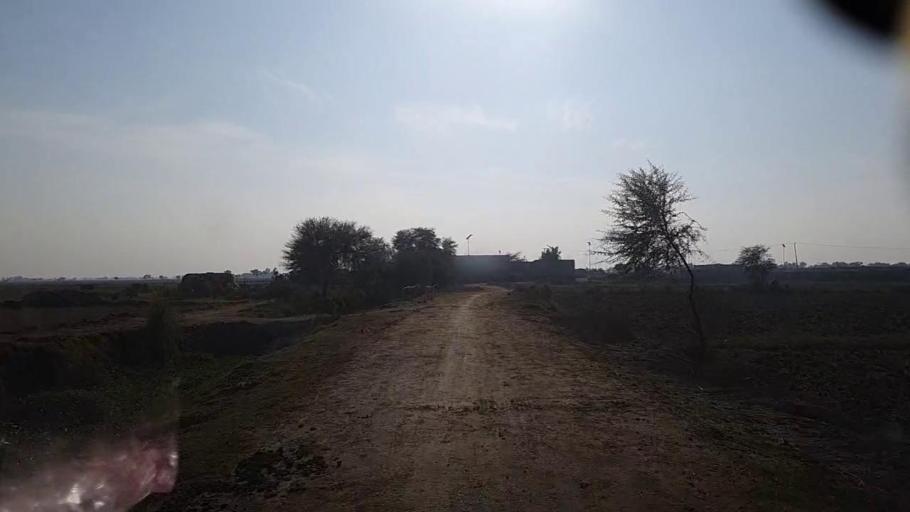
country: PK
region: Sindh
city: Jacobabad
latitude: 28.2910
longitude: 68.5568
